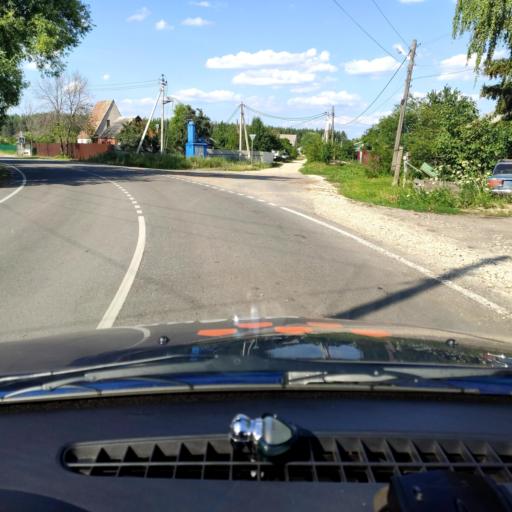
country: RU
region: Voronezj
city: Devitsa
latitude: 51.6496
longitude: 38.9724
